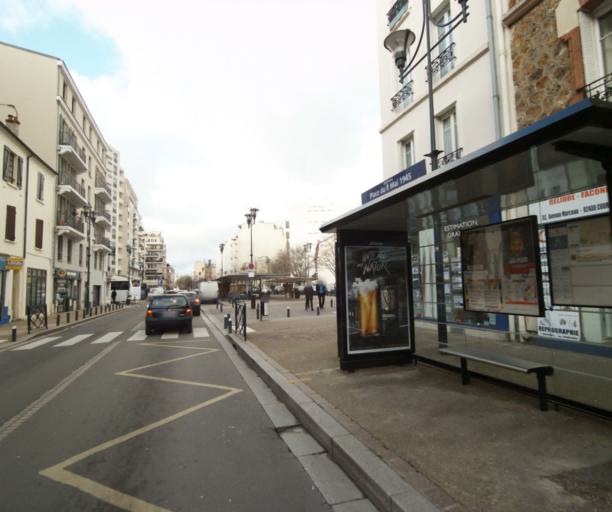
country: FR
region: Ile-de-France
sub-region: Departement des Hauts-de-Seine
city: La Garenne-Colombes
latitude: 48.9004
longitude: 2.2450
